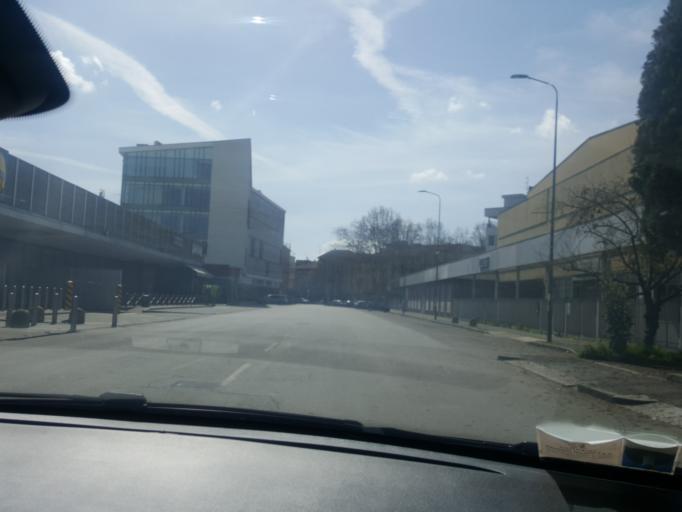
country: IT
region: Lombardy
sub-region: Citta metropolitana di Milano
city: Novate Milanese
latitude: 45.4981
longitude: 9.1373
